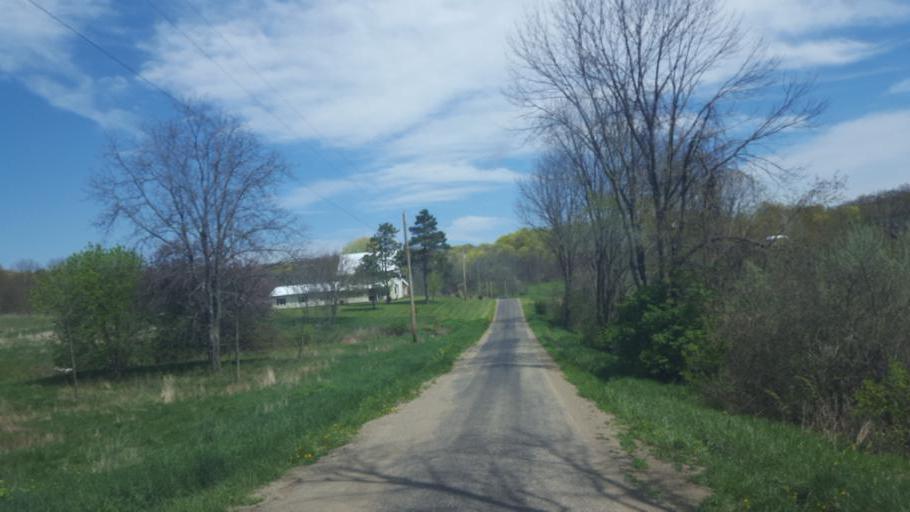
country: US
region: Ohio
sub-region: Ashland County
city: Ashland
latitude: 40.7842
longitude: -82.3295
